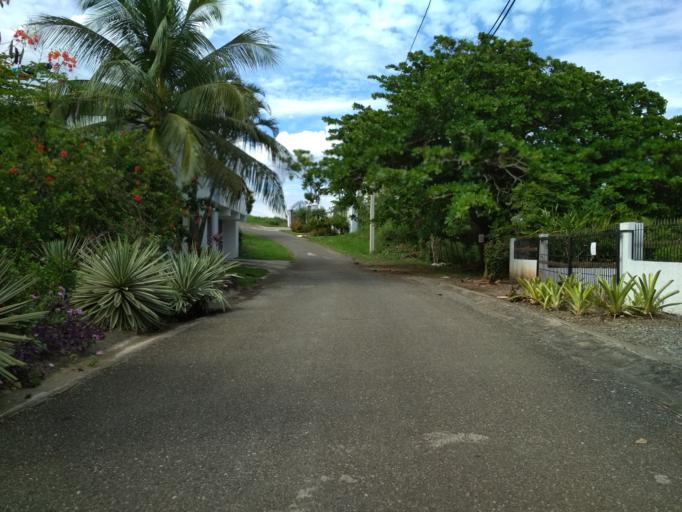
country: DO
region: Puerto Plata
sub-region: Puerto Plata
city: Puerto Plata
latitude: 19.8086
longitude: -70.7089
